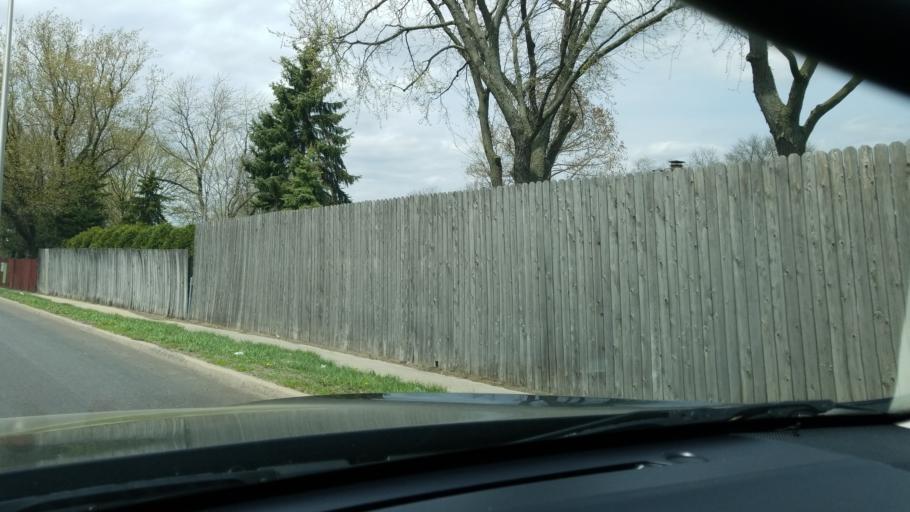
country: US
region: Illinois
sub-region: Cook County
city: Rolling Meadows
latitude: 42.0552
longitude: -87.9989
